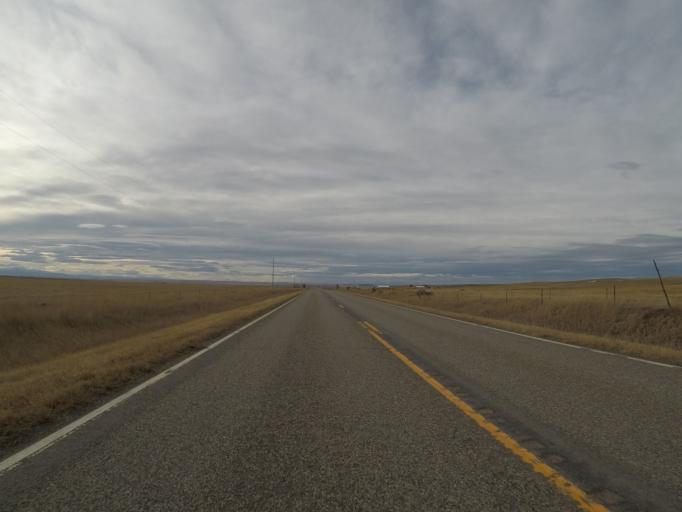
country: US
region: Montana
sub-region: Yellowstone County
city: Laurel
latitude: 45.8565
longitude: -108.8222
